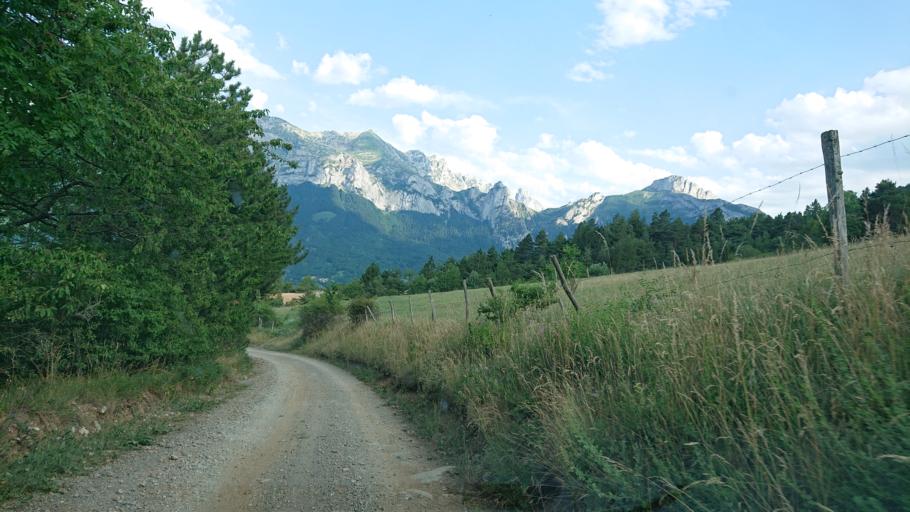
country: FR
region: Rhone-Alpes
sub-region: Departement de l'Isere
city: Mens
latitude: 44.7966
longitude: 5.8969
